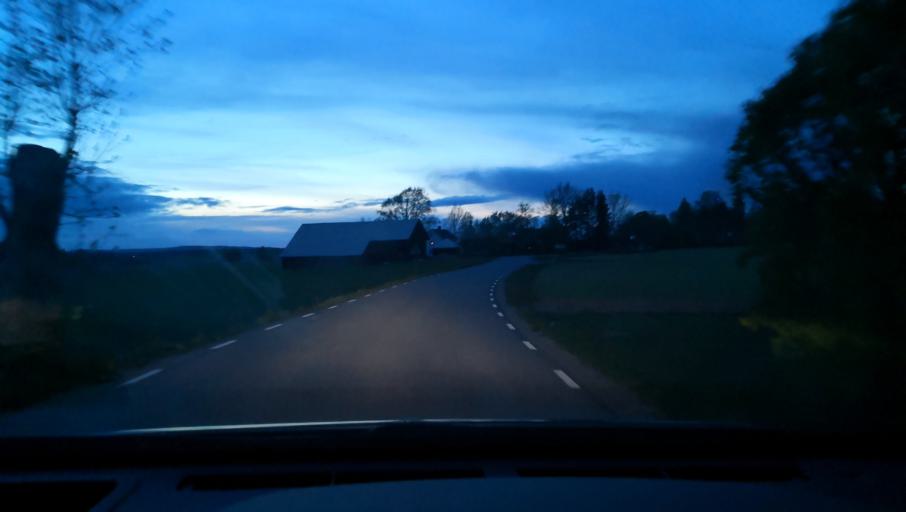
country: SE
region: OErebro
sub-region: Orebro Kommun
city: Vintrosa
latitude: 59.1522
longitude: 15.0041
